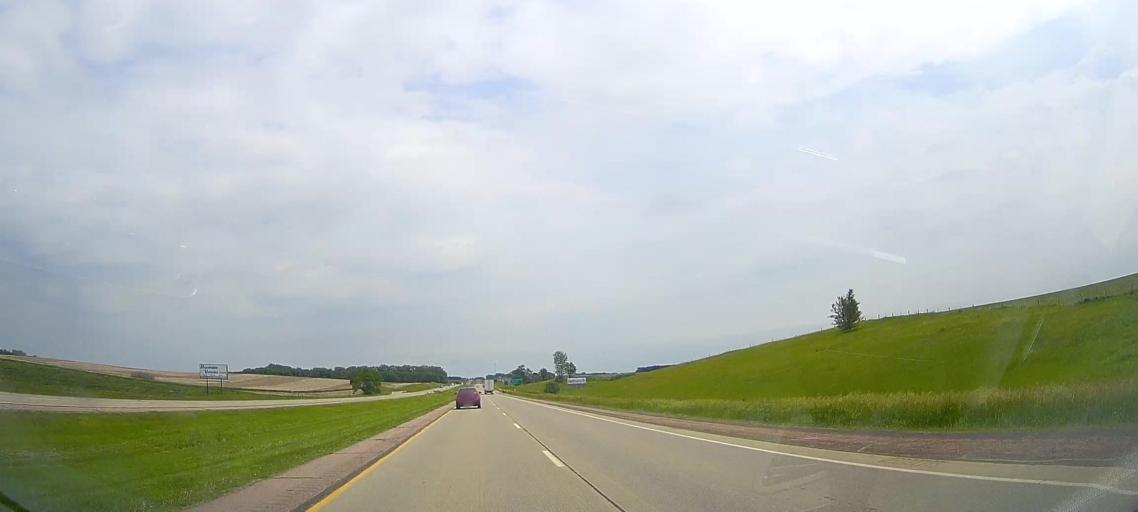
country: US
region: South Dakota
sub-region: Minnehaha County
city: Crooks
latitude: 43.6085
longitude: -96.8449
